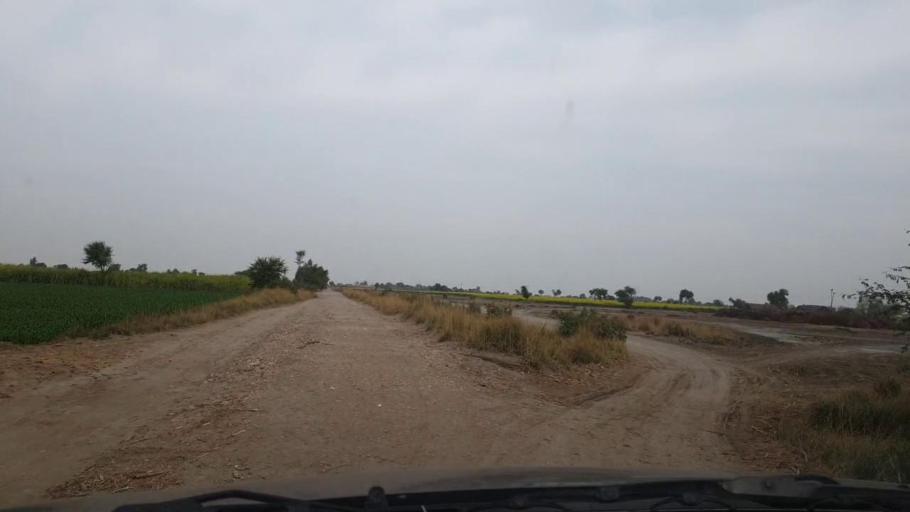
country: PK
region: Sindh
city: Sanghar
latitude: 26.1115
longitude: 68.8963
